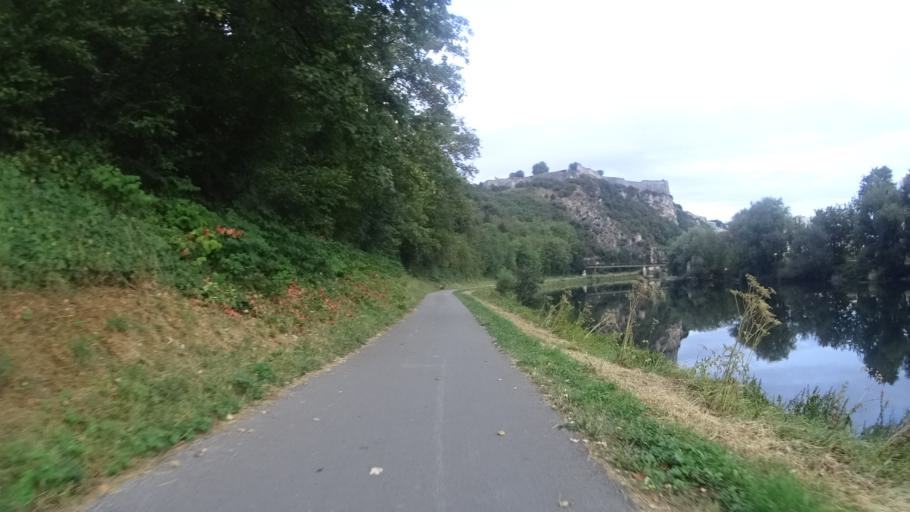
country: FR
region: Franche-Comte
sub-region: Departement du Doubs
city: Morre
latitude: 47.2259
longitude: 6.0441
